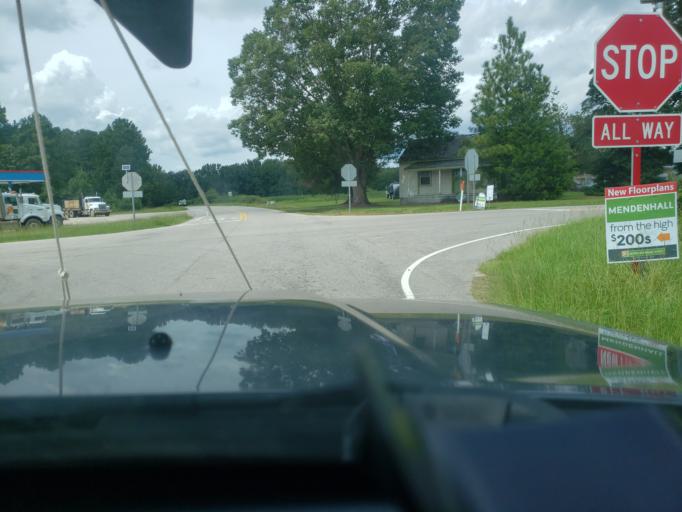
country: US
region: North Carolina
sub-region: Wake County
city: Rolesville
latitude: 35.8924
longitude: -78.4289
